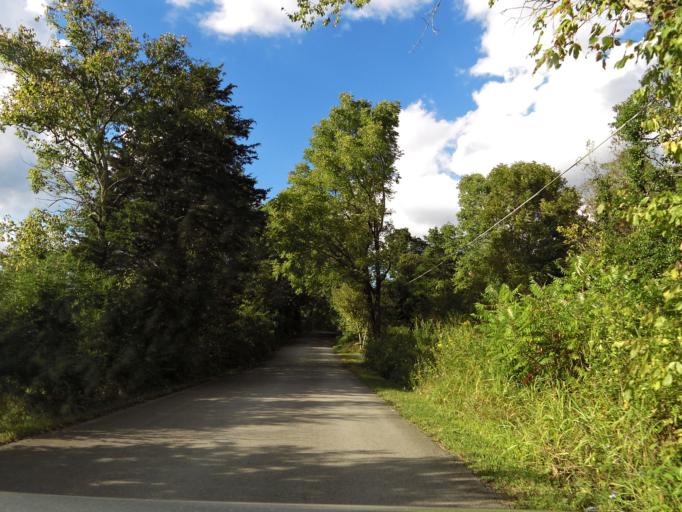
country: US
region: Tennessee
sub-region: Knox County
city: Mascot
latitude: 36.1003
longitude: -83.7870
